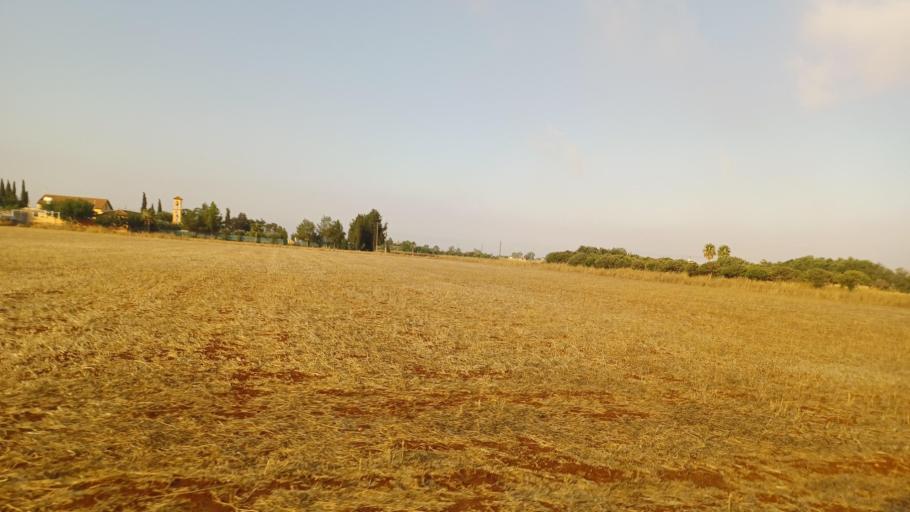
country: CY
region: Ammochostos
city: Avgorou
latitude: 35.0360
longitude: 33.8654
